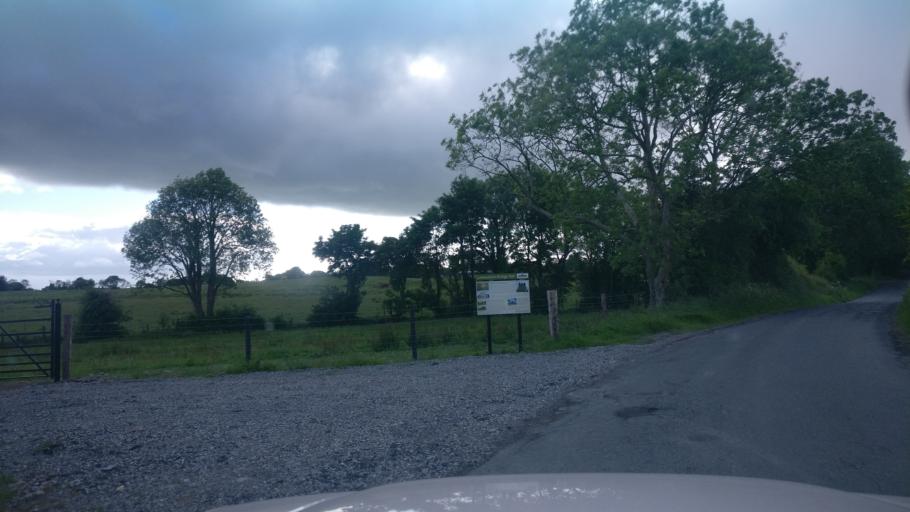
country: IE
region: Connaught
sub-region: County Galway
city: Ballinasloe
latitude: 53.2327
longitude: -8.1945
